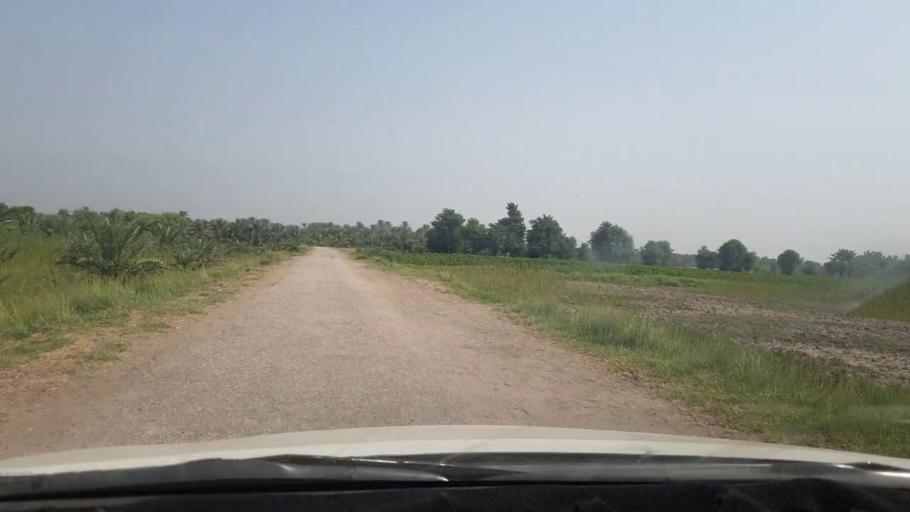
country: PK
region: Sindh
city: Rohri
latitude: 27.6133
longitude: 68.8978
